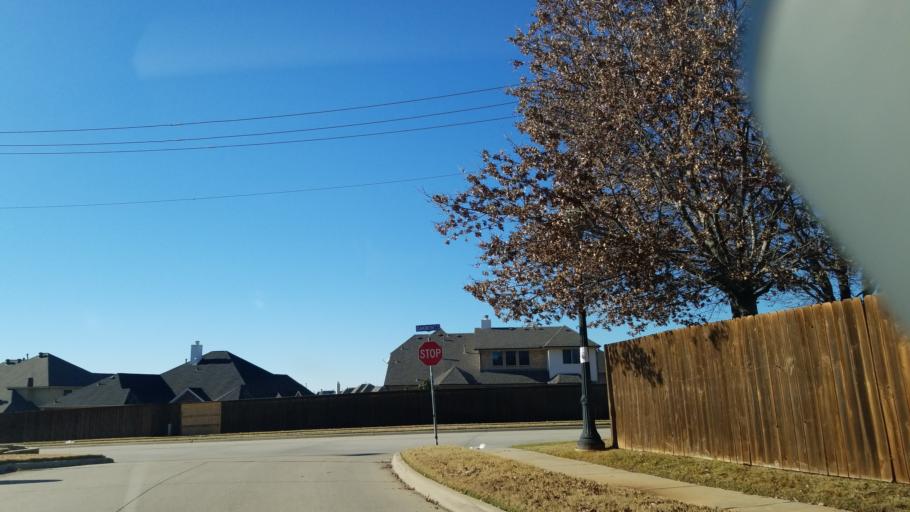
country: US
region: Texas
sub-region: Denton County
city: Corinth
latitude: 33.1387
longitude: -97.0879
